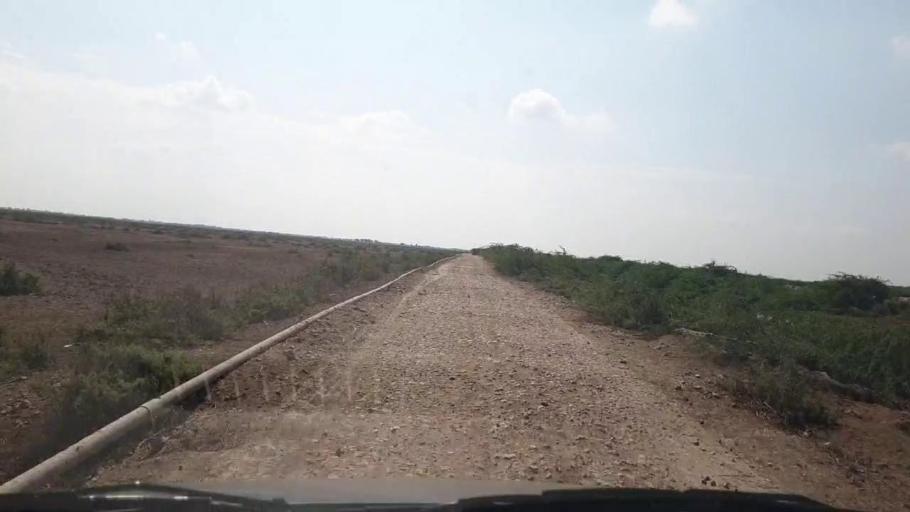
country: PK
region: Sindh
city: Badin
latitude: 24.5060
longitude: 68.6081
